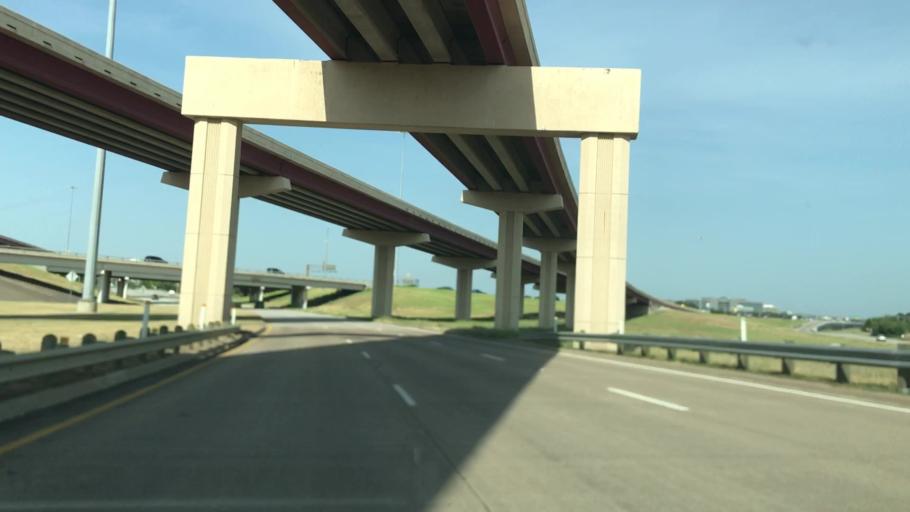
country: US
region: Texas
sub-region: Dallas County
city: Farmers Branch
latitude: 32.9104
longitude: -96.9432
